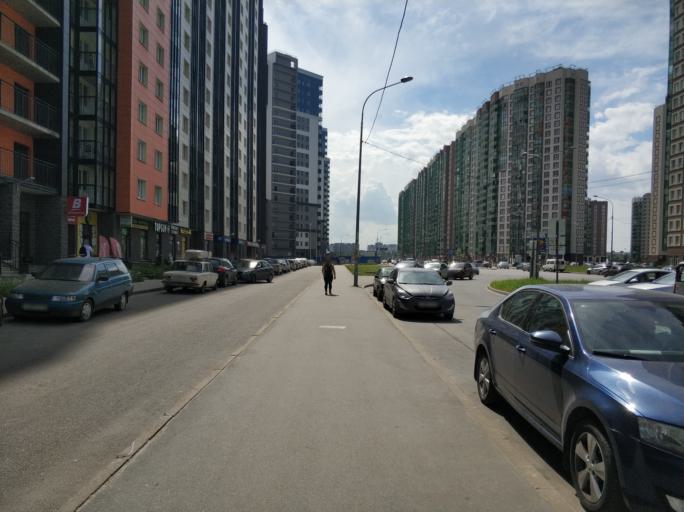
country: RU
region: Leningrad
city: Murino
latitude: 60.0550
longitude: 30.4272
